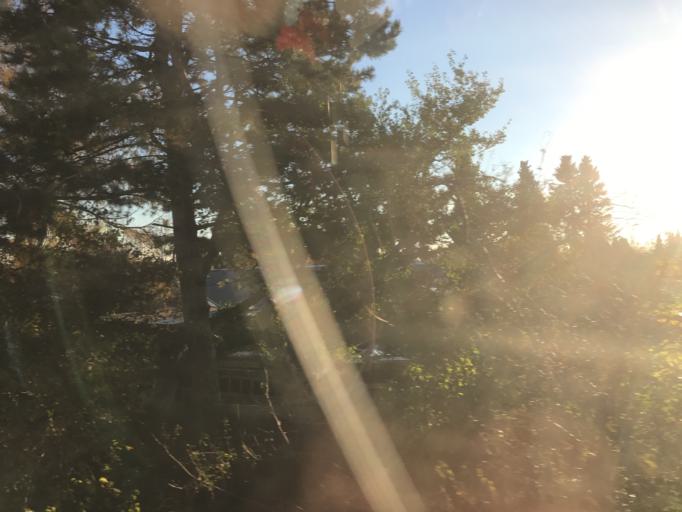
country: DK
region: Capital Region
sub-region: Brondby Kommune
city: Brondbyvester
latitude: 55.6215
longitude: 12.4132
